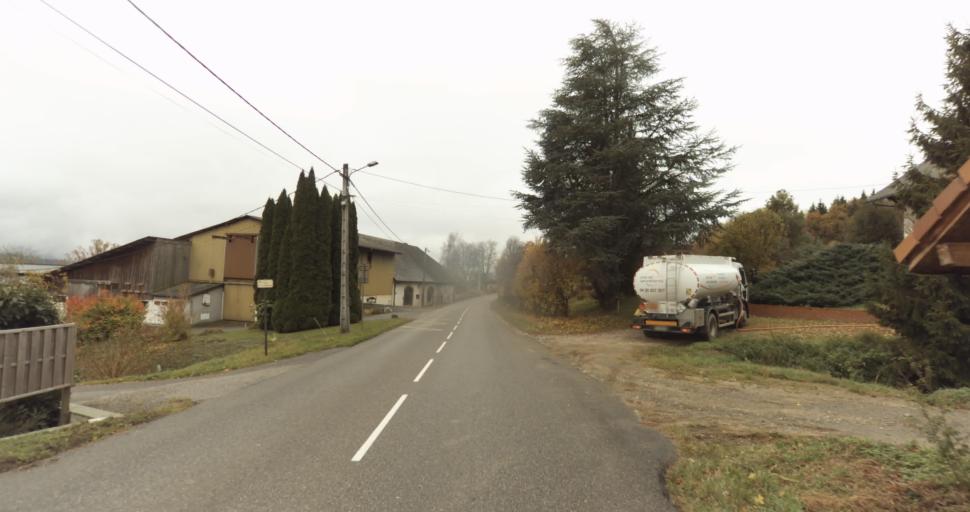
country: FR
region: Rhone-Alpes
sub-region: Departement de la Haute-Savoie
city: Evires
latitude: 46.0333
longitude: 6.2085
